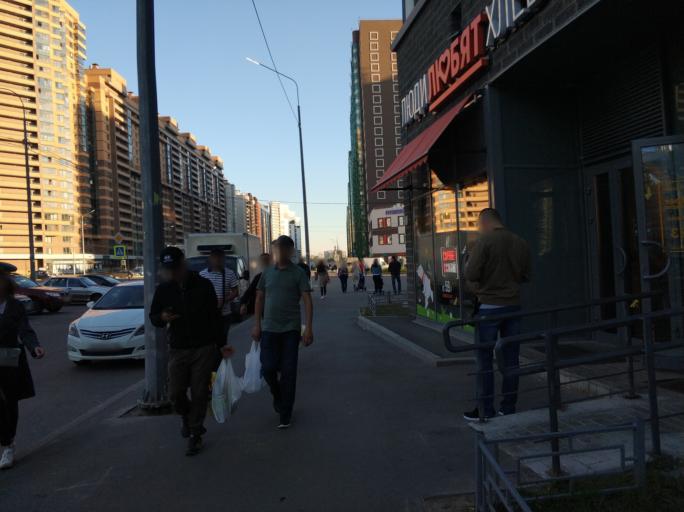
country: RU
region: Leningrad
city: Murino
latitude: 60.0586
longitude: 30.4293
